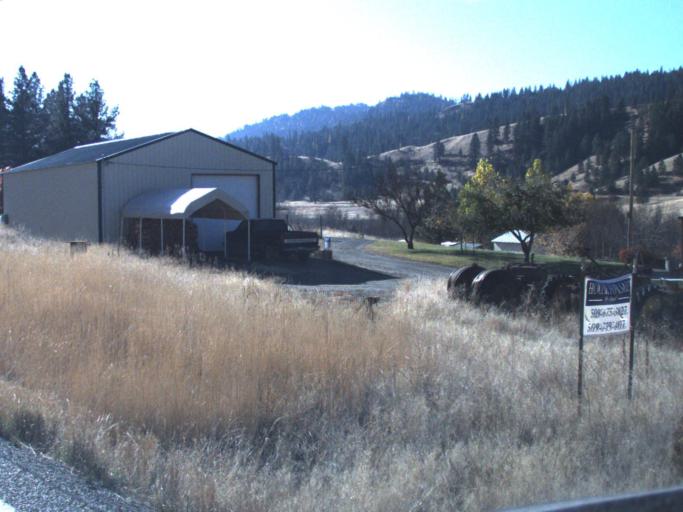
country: US
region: Washington
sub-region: Ferry County
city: Republic
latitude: 48.8516
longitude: -118.6014
